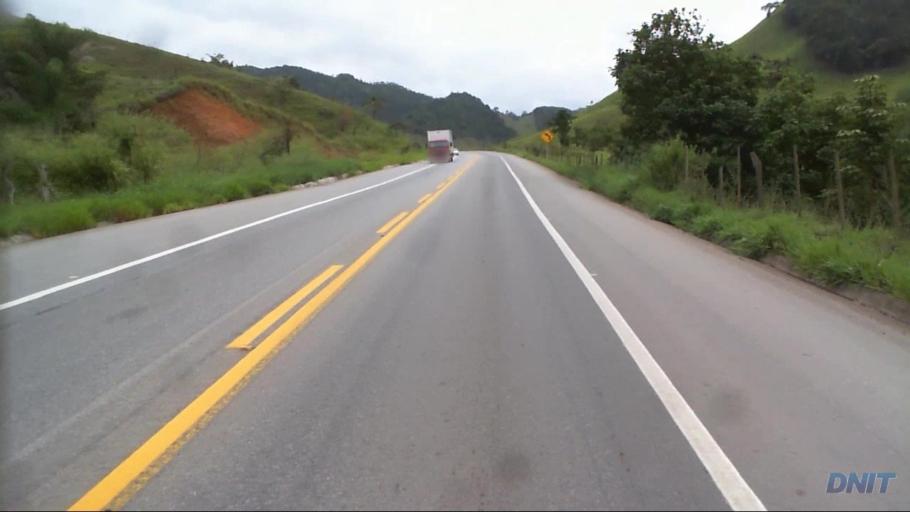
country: BR
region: Minas Gerais
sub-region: Timoteo
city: Timoteo
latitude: -19.6213
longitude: -42.8408
